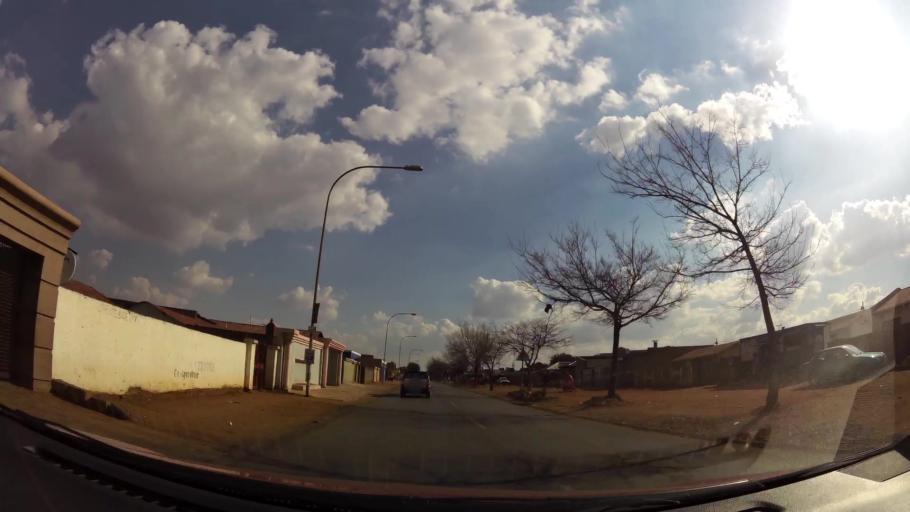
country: ZA
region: Gauteng
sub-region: City of Johannesburg Metropolitan Municipality
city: Soweto
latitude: -26.2227
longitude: 27.8697
